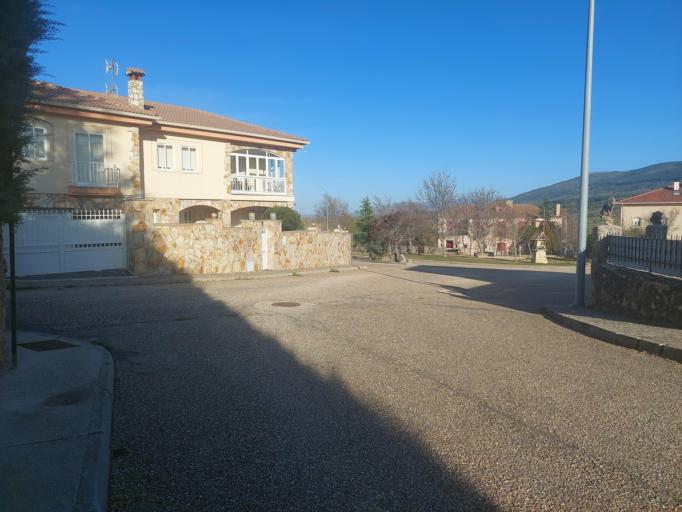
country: ES
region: Castille and Leon
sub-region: Provincia de Segovia
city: Pradena
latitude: 41.1362
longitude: -3.6918
